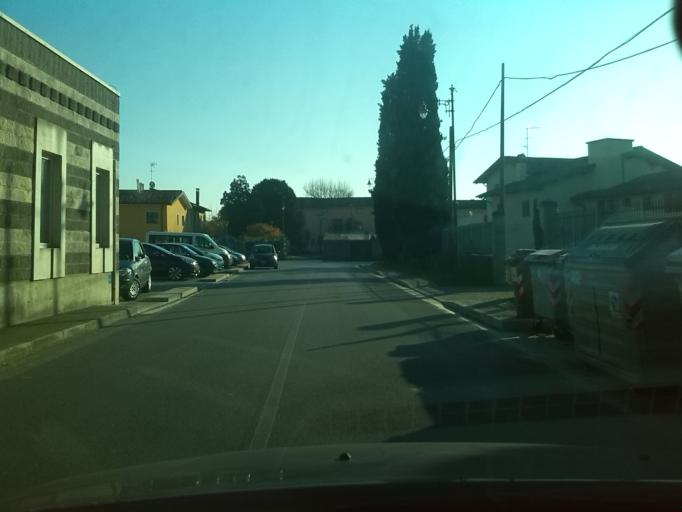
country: IT
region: Friuli Venezia Giulia
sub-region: Provincia di Udine
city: Santa Maria la Longa
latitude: 45.9348
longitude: 13.2947
